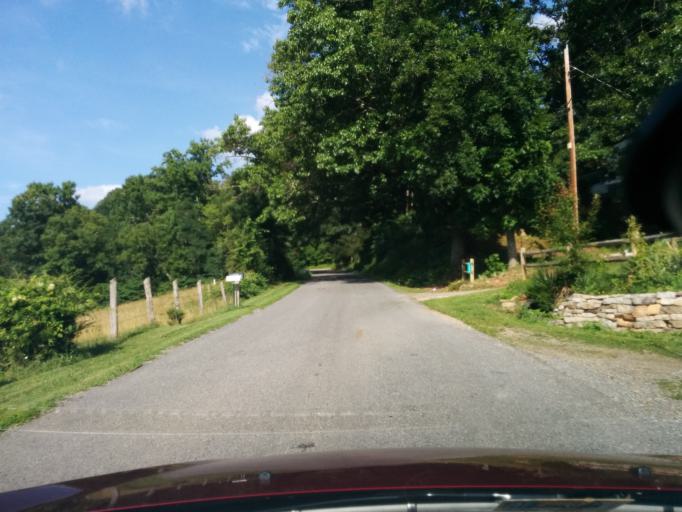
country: US
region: Virginia
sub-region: City of Lexington
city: Lexington
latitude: 37.7736
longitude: -79.4834
